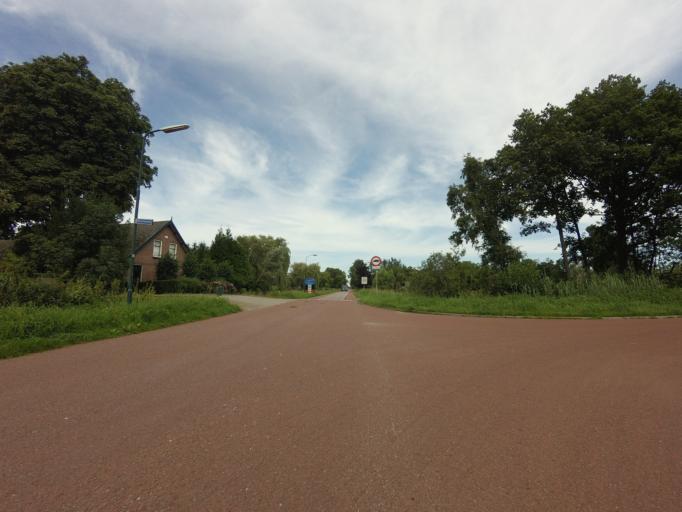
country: NL
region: Utrecht
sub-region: Stichtse Vecht
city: Breukelen
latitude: 52.1612
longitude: 4.9576
